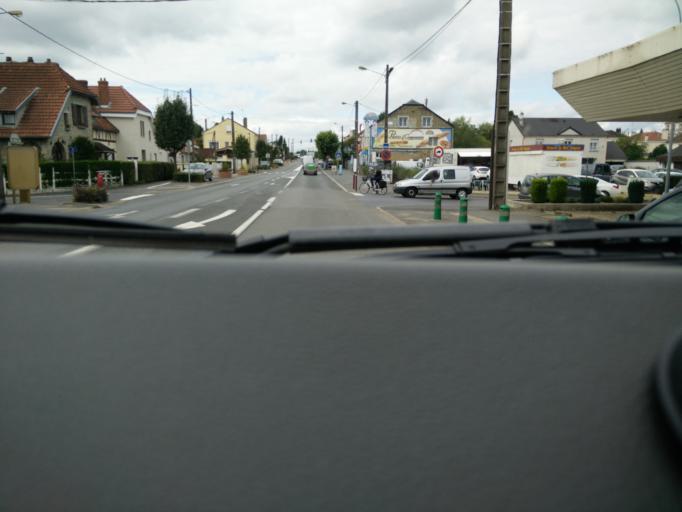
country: FR
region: Champagne-Ardenne
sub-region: Departement des Ardennes
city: Warcq
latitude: 49.7787
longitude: 4.6948
